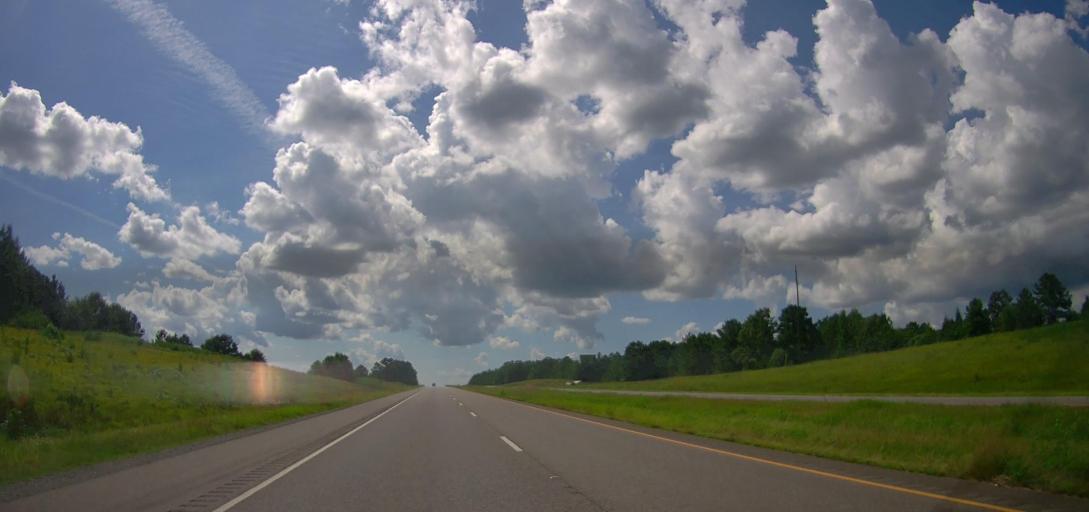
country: US
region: Alabama
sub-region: Pickens County
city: Reform
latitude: 33.3893
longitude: -88.0390
